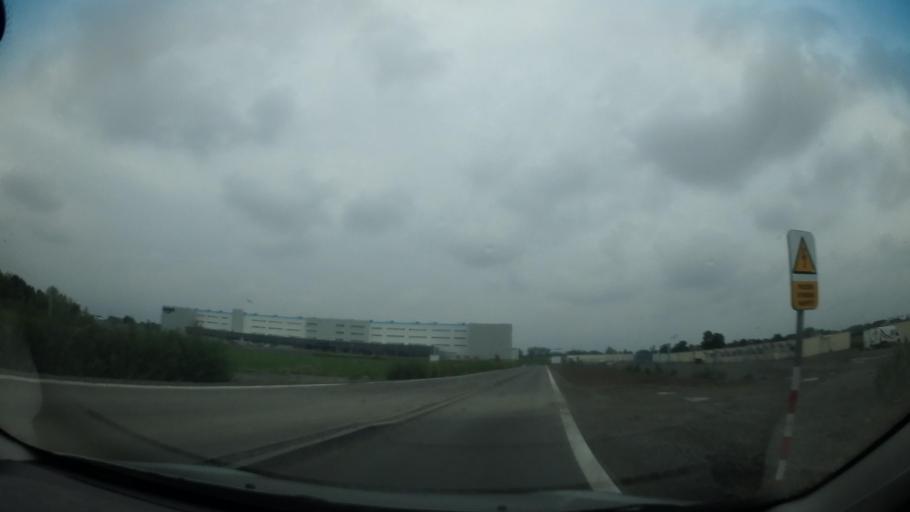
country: CZ
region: Olomoucky
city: Kojetin
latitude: 49.3370
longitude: 17.3097
